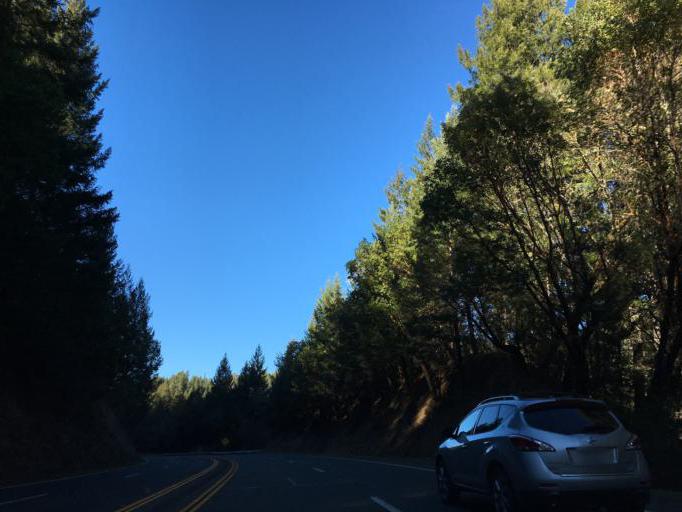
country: US
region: California
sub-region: Mendocino County
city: Brooktrails
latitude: 39.5392
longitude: -123.4176
